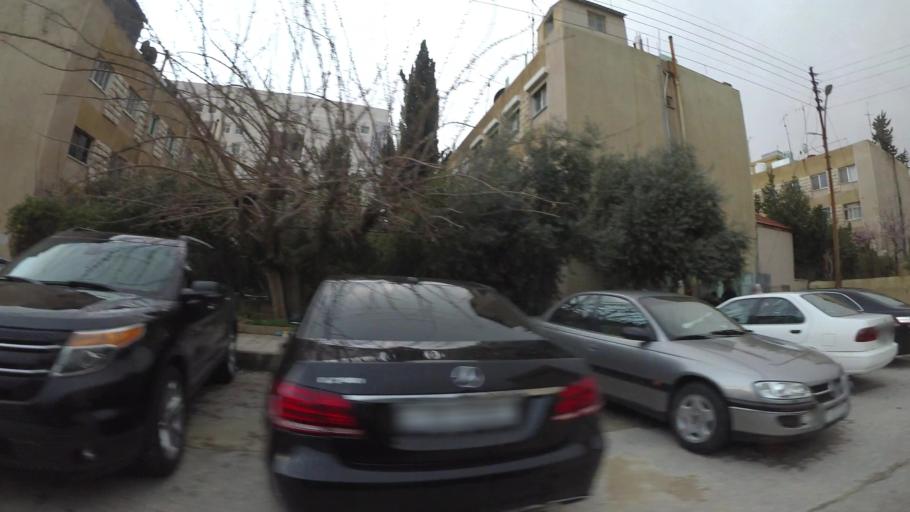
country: JO
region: Amman
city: Al Jubayhah
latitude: 31.9681
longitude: 35.8807
